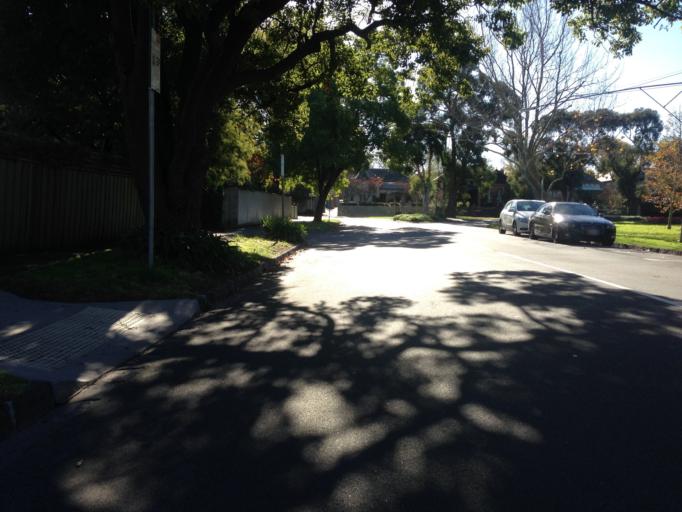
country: AU
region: Victoria
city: Balwyn
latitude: -37.8261
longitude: 145.0629
